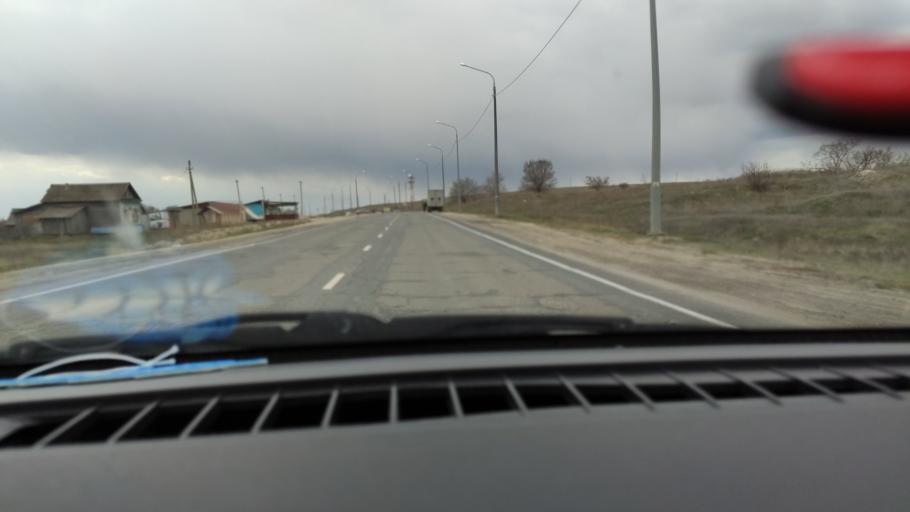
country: RU
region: Saratov
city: Sinodskoye
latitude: 52.0862
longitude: 46.8025
